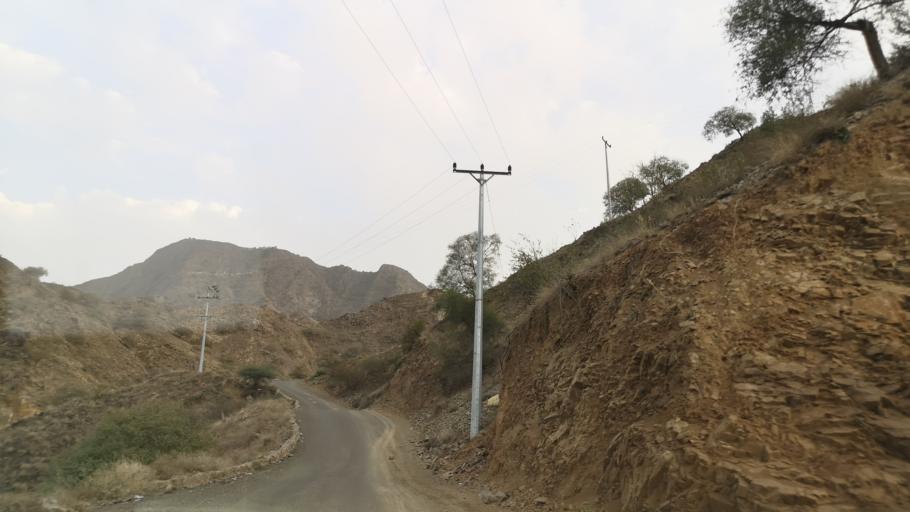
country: YE
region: Sa'dah
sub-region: Monabbih
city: Suq al Khamis
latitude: 17.3276
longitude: 43.1451
